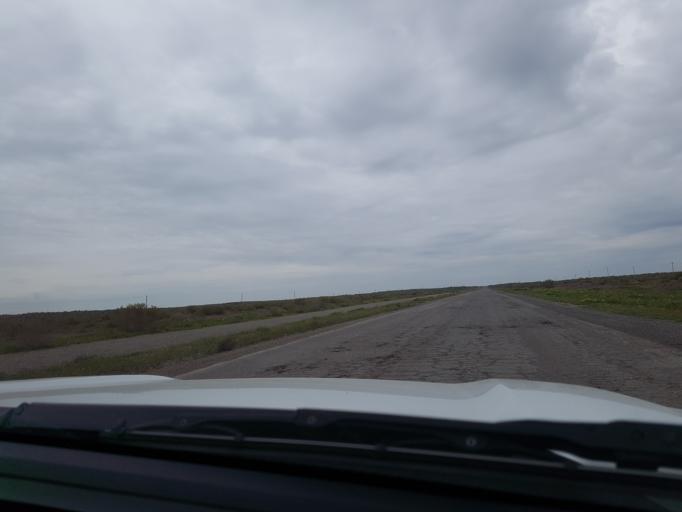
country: TM
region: Mary
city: Bayramaly
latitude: 37.9255
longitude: 62.6250
